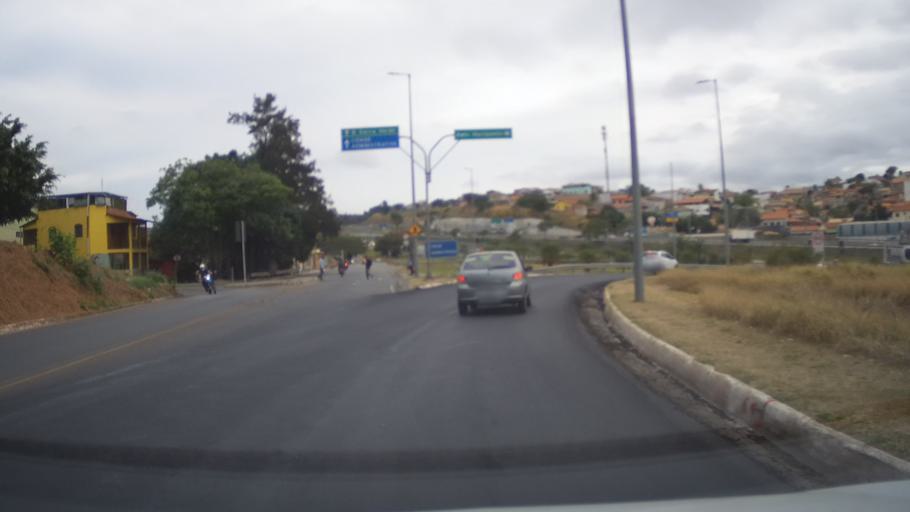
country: BR
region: Minas Gerais
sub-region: Santa Luzia
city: Santa Luzia
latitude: -19.7996
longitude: -43.9512
